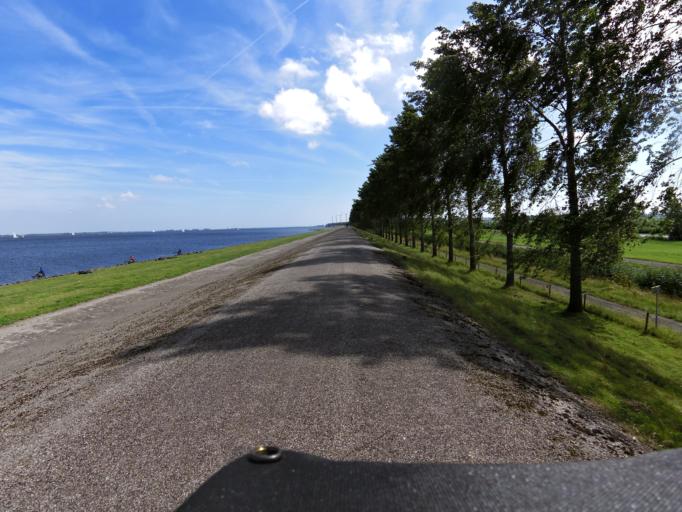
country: NL
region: South Holland
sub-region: Gemeente Goeree-Overflakkee
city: Middelharnis
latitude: 51.7666
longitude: 4.2010
